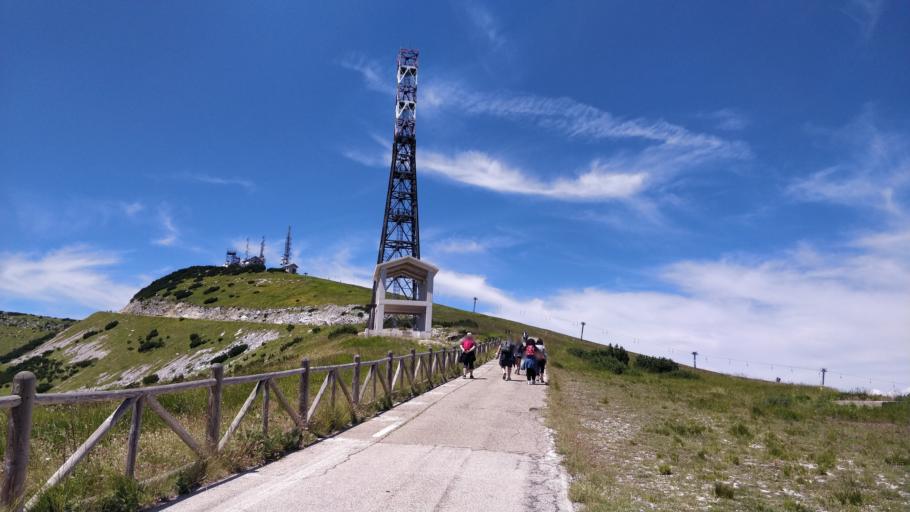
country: IT
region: Abruzzo
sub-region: Provincia di Chieti
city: Pretoro
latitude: 42.1585
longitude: 14.1325
